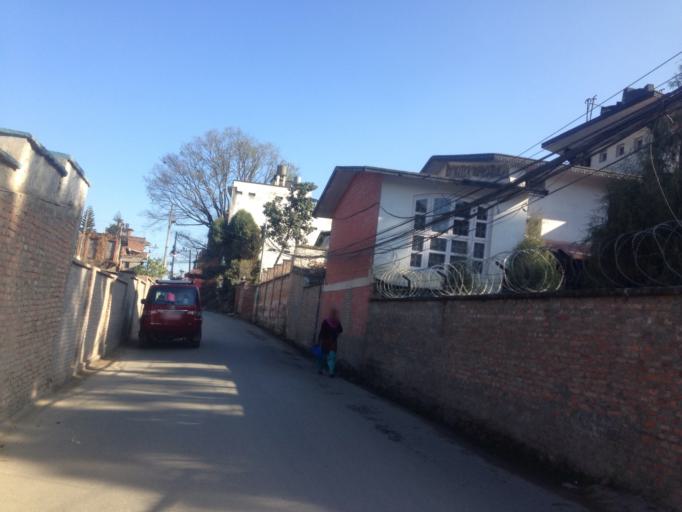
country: NP
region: Central Region
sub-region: Bagmati Zone
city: Kathmandu
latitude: 27.7222
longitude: 85.3347
